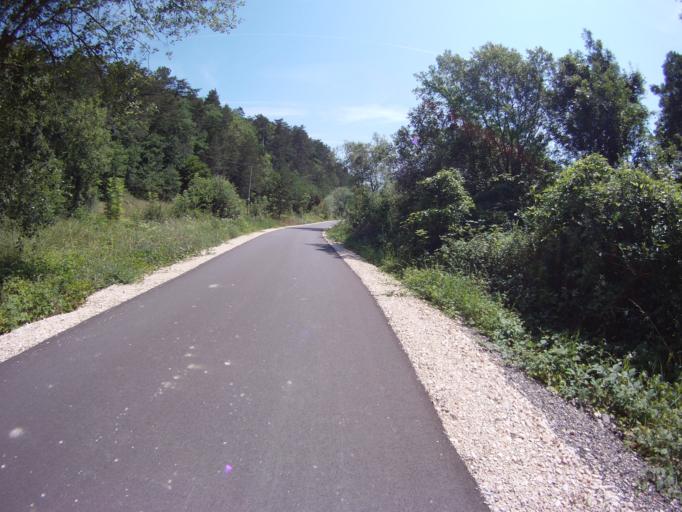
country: FR
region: Lorraine
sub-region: Departement de Meurthe-et-Moselle
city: Liverdun
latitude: 48.7588
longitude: 6.0401
